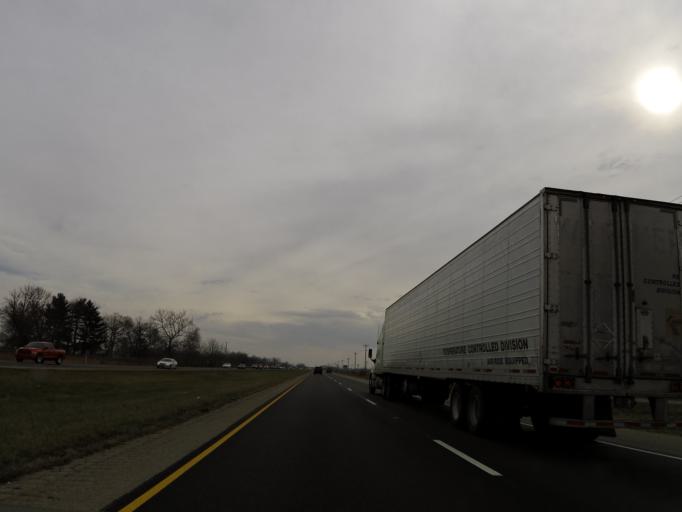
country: US
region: Indiana
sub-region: Shelby County
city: Shelbyville
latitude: 39.5749
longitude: -85.8099
